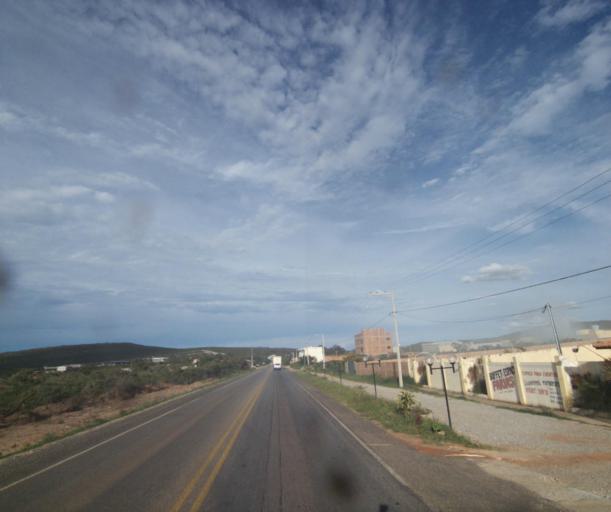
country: BR
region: Bahia
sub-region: Caetite
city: Caetite
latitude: -14.0661
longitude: -42.5276
